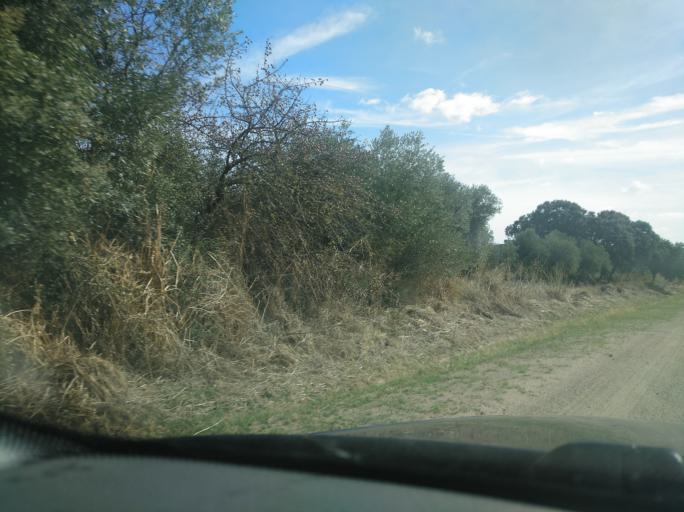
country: PT
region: Portalegre
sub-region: Campo Maior
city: Campo Maior
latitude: 39.0463
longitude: -7.0474
